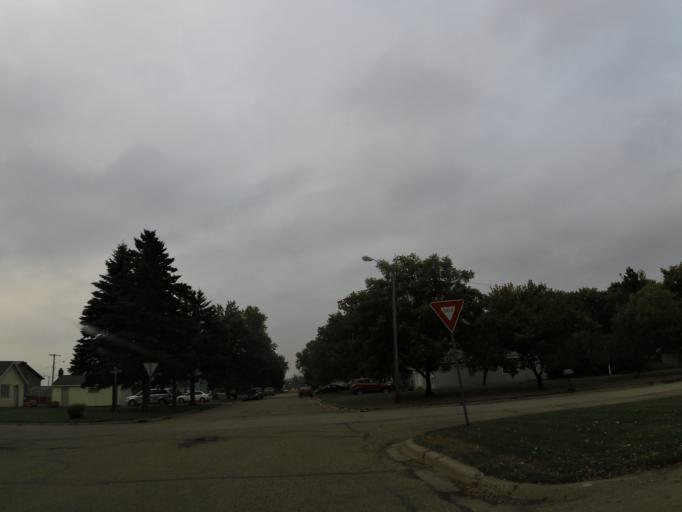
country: US
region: North Dakota
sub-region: Walsh County
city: Grafton
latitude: 48.5660
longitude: -97.1763
